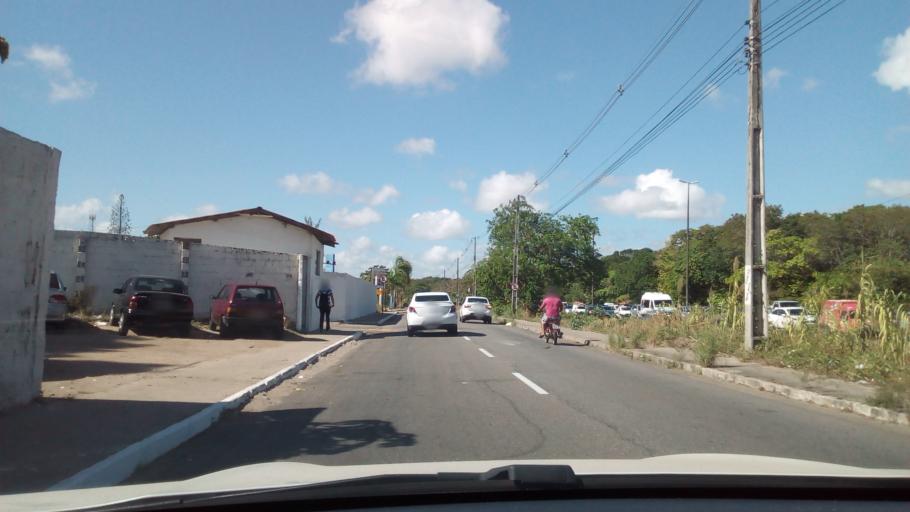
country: BR
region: Paraiba
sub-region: Joao Pessoa
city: Joao Pessoa
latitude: -7.1532
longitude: -34.8546
